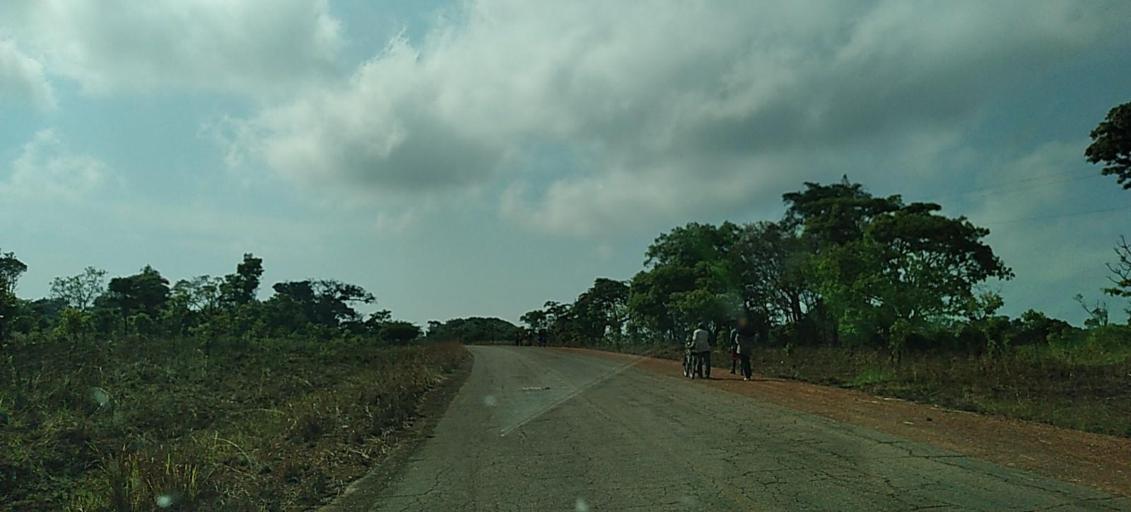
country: ZM
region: North-Western
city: Mwinilunga
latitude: -11.7642
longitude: 24.9990
